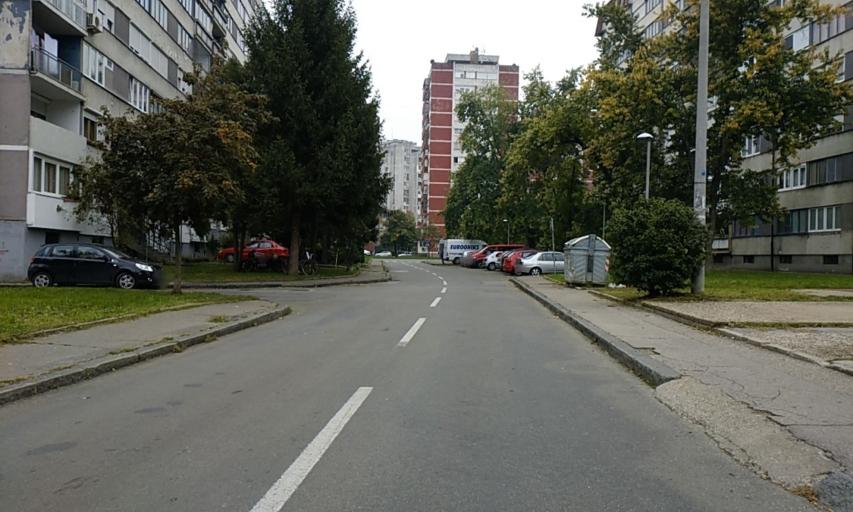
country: BA
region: Republika Srpska
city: Starcevica
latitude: 44.7723
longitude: 17.2058
